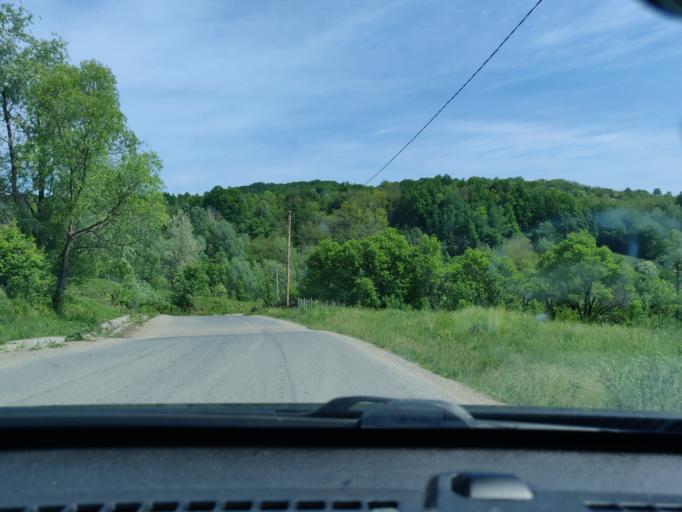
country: RO
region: Vrancea
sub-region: Comuna Vidra
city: Vidra
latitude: 45.9235
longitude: 26.8956
